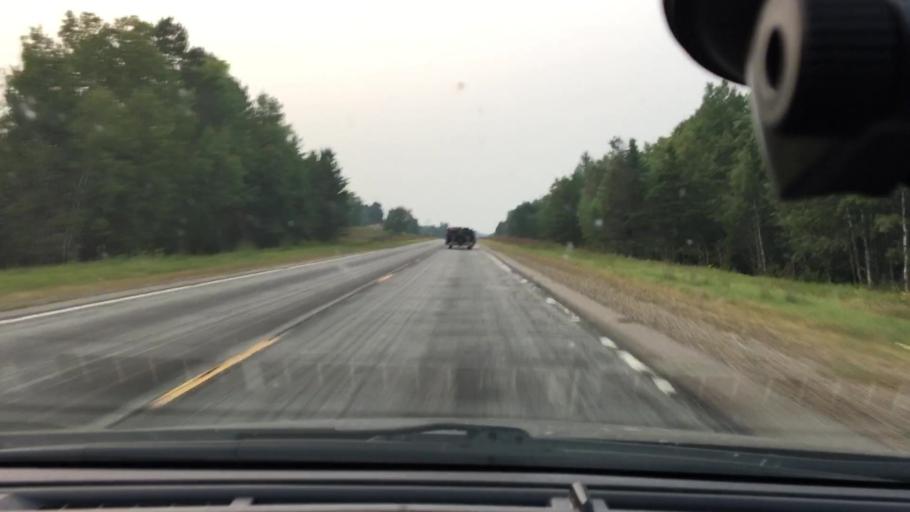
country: US
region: Minnesota
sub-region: Crow Wing County
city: Cross Lake
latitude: 46.6820
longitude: -93.9533
